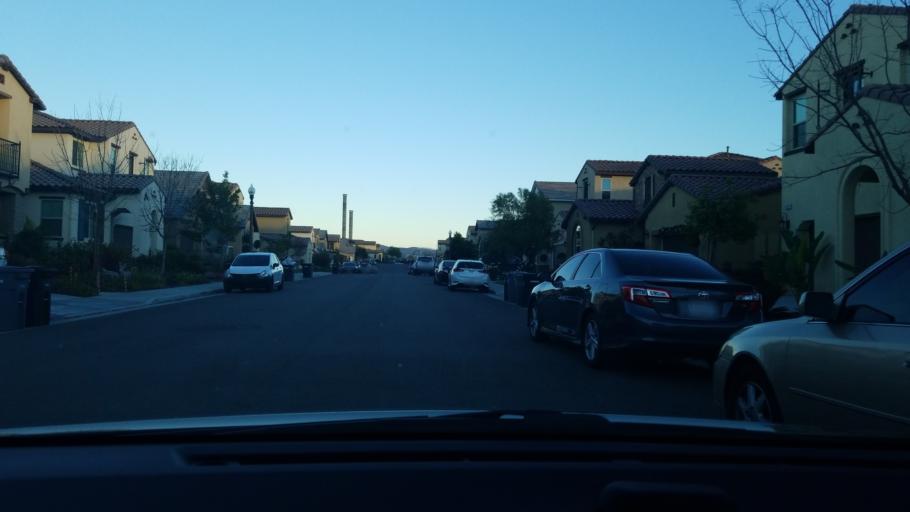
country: US
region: California
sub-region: Riverside County
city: Murrieta Hot Springs
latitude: 33.5525
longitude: -117.1059
